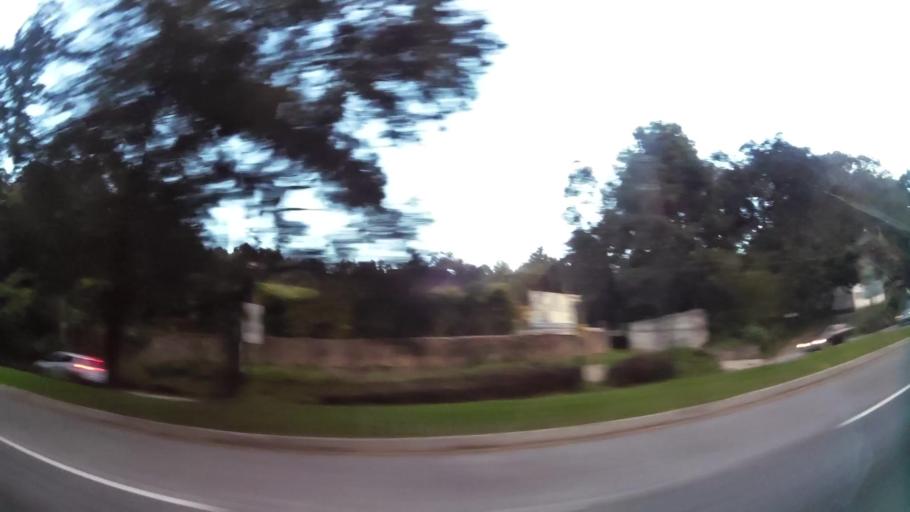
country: GT
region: Sacatepequez
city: San Lucas Sacatepequez
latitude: 14.6016
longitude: -90.6445
